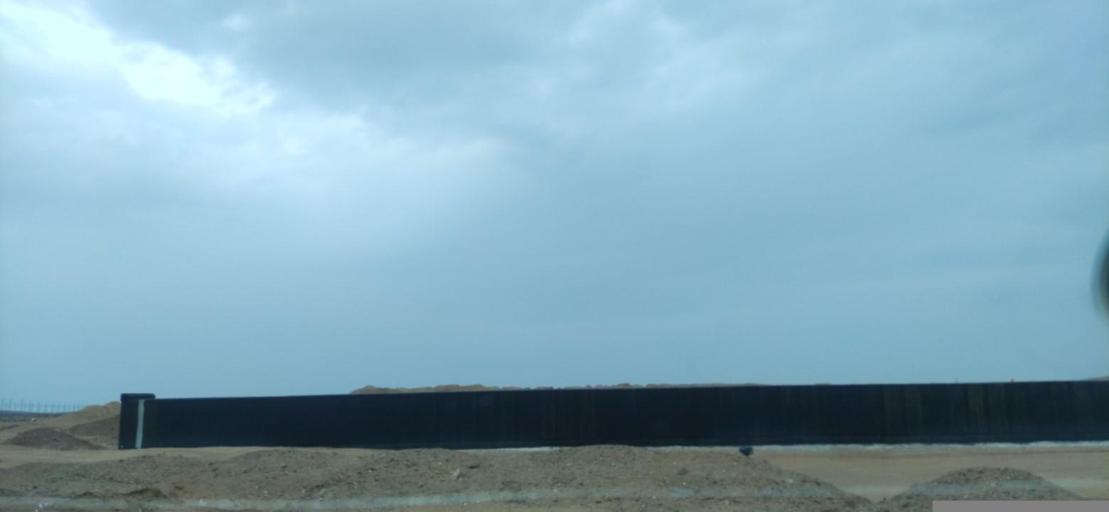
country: KZ
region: Qaraghandy
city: Saryshaghan
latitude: 46.1409
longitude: 73.6069
